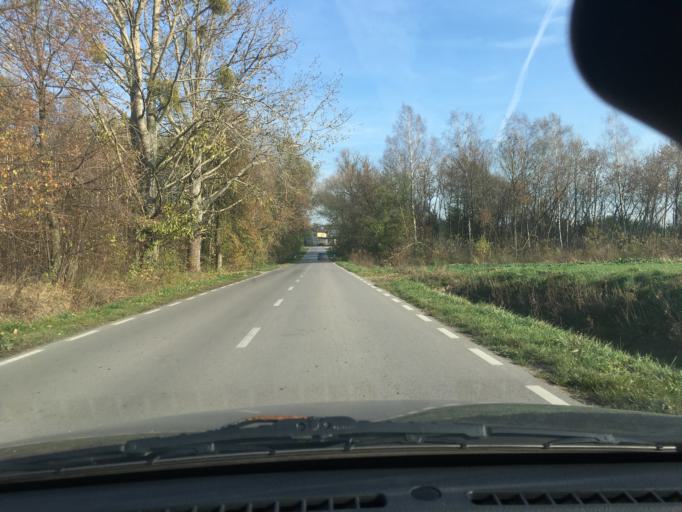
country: PL
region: Masovian Voivodeship
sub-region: Powiat plocki
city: Bodzanow
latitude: 52.4914
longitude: 20.0278
